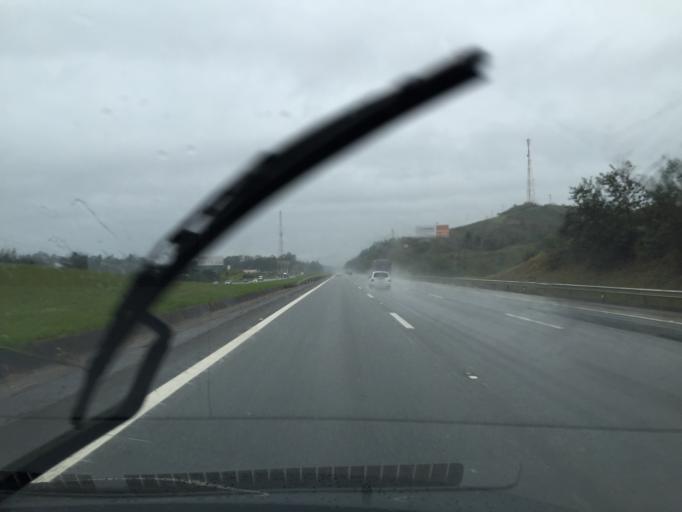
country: BR
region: Sao Paulo
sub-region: Sao Roque
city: Sao Roque
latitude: -23.4208
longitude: -47.1861
